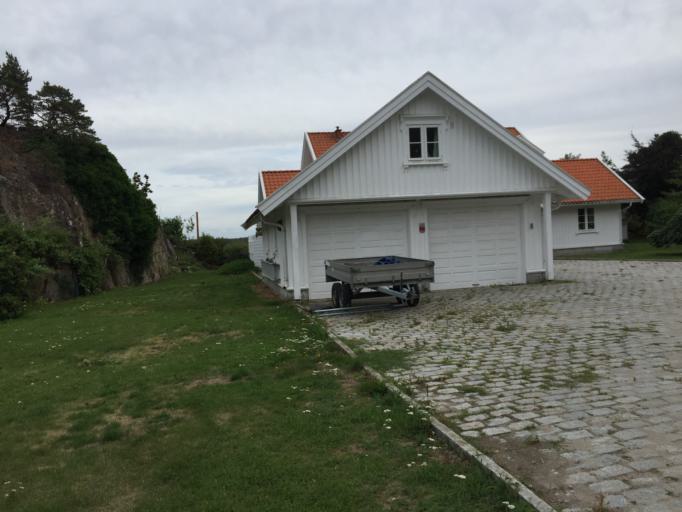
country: NO
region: Ostfold
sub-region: Hvaler
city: Skjaerhalden
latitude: 59.0327
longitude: 11.0561
